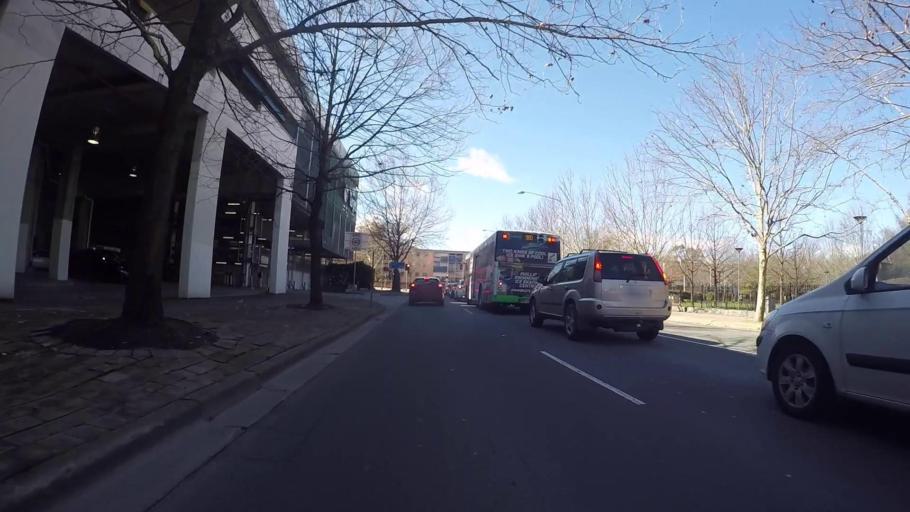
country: AU
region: Australian Capital Territory
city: Canberra
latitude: -35.2806
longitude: 149.1352
